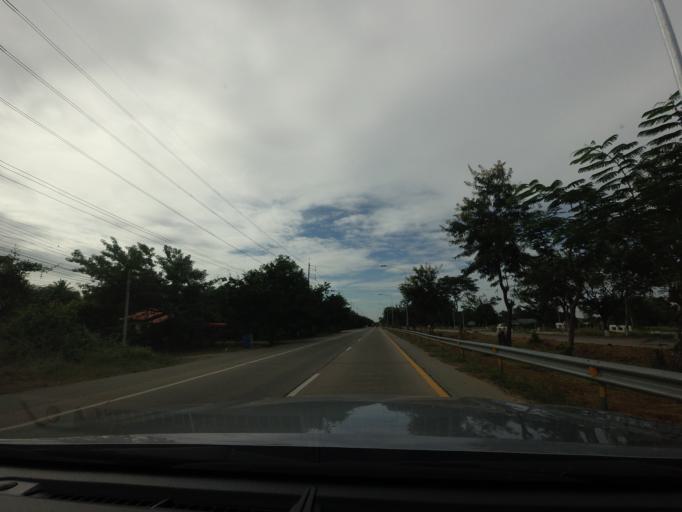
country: TH
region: Suphan Buri
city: Doem Bang Nang Buat
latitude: 14.9020
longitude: 100.0912
